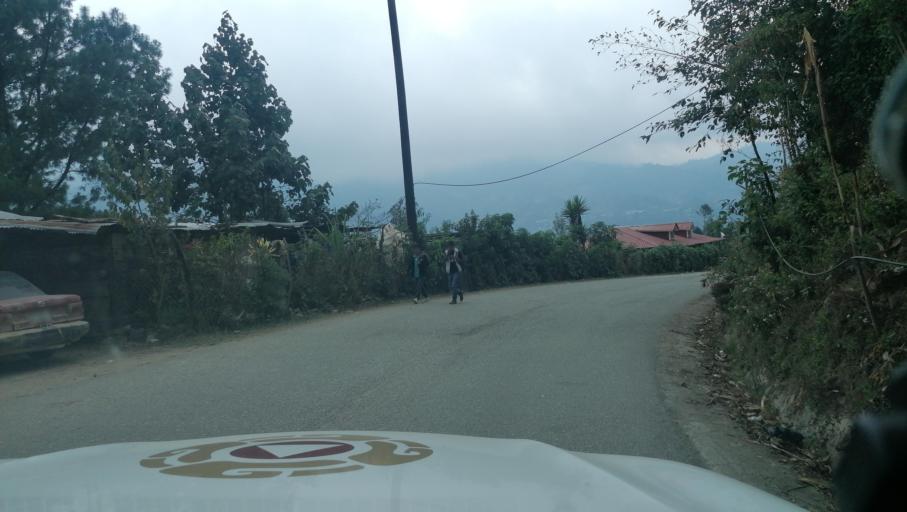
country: GT
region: San Marcos
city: Tacana
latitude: 15.2037
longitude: -92.1848
